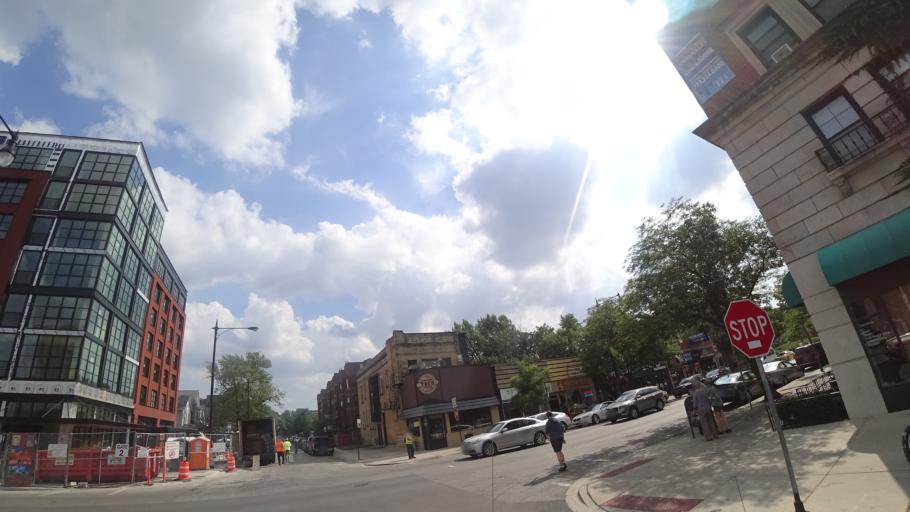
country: US
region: Illinois
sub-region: Cook County
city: Chicago
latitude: 41.7997
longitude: -87.5917
